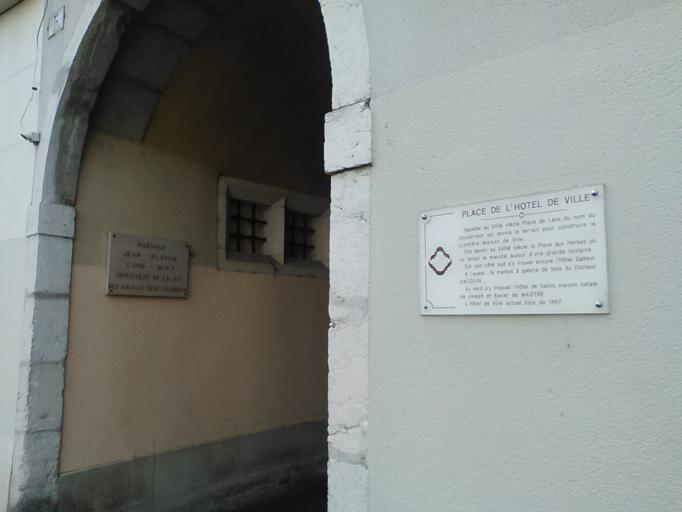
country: FR
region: Rhone-Alpes
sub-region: Departement de la Savoie
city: Chambery
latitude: 45.5661
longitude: 5.9206
